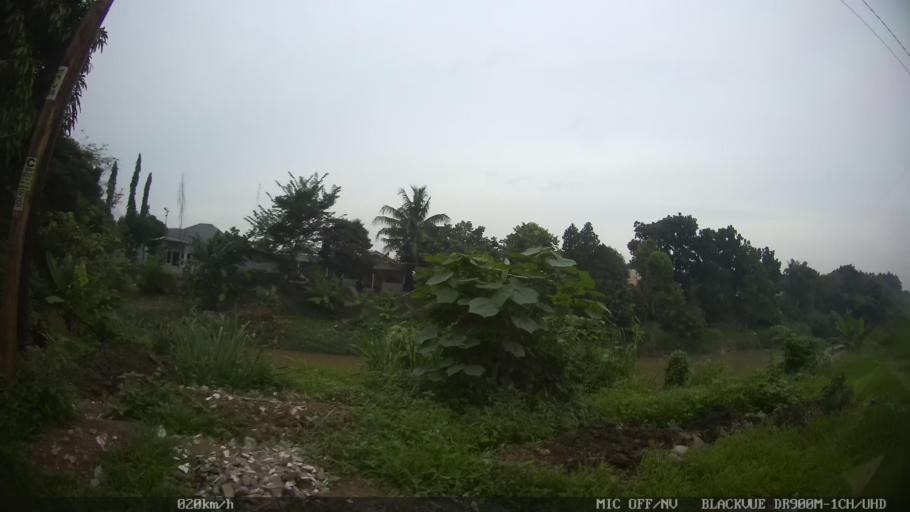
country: ID
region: North Sumatra
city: Deli Tua
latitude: 3.5442
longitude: 98.7154
